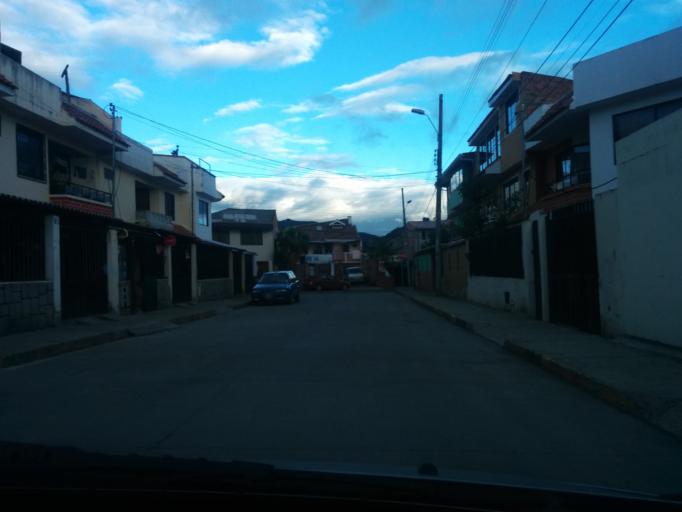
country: EC
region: Azuay
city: Cuenca
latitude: -2.8851
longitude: -78.9687
